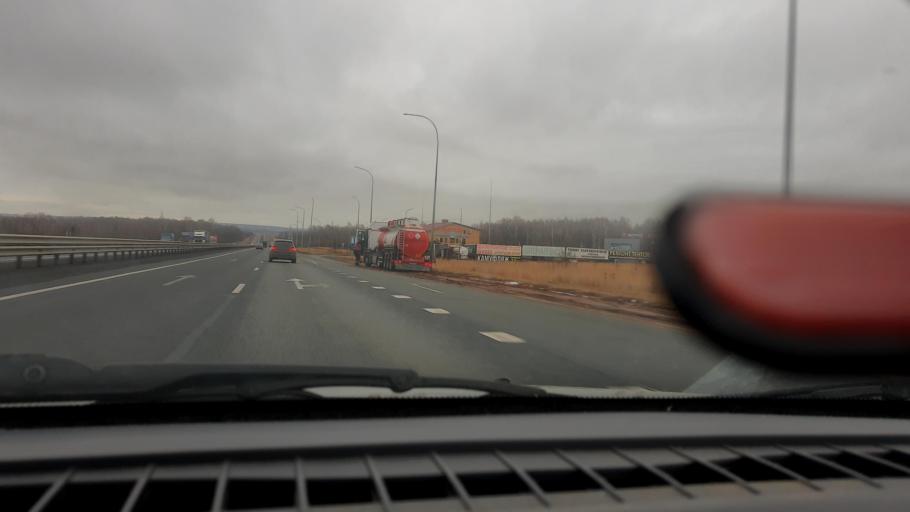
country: RU
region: Nizjnij Novgorod
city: Burevestnik
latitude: 56.1447
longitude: 43.7546
